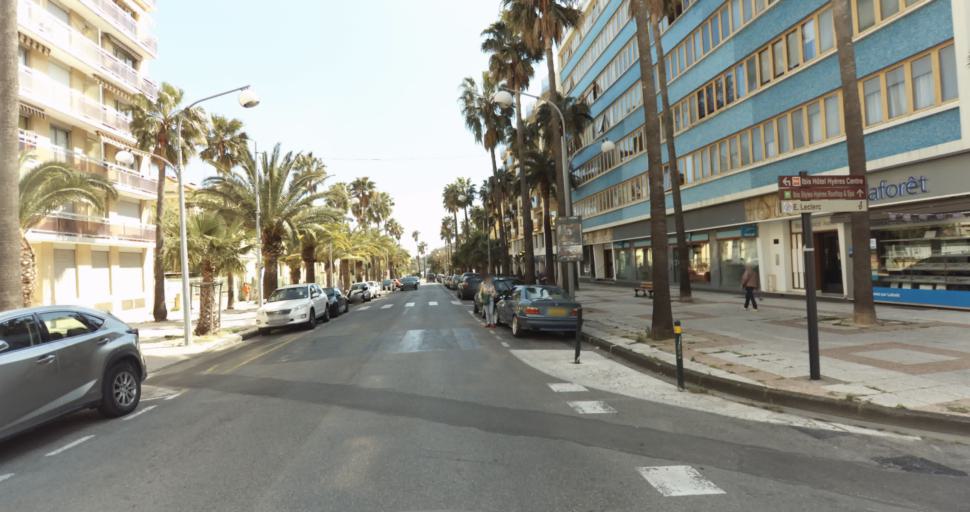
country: FR
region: Provence-Alpes-Cote d'Azur
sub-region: Departement du Var
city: Hyeres
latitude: 43.1152
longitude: 6.1286
